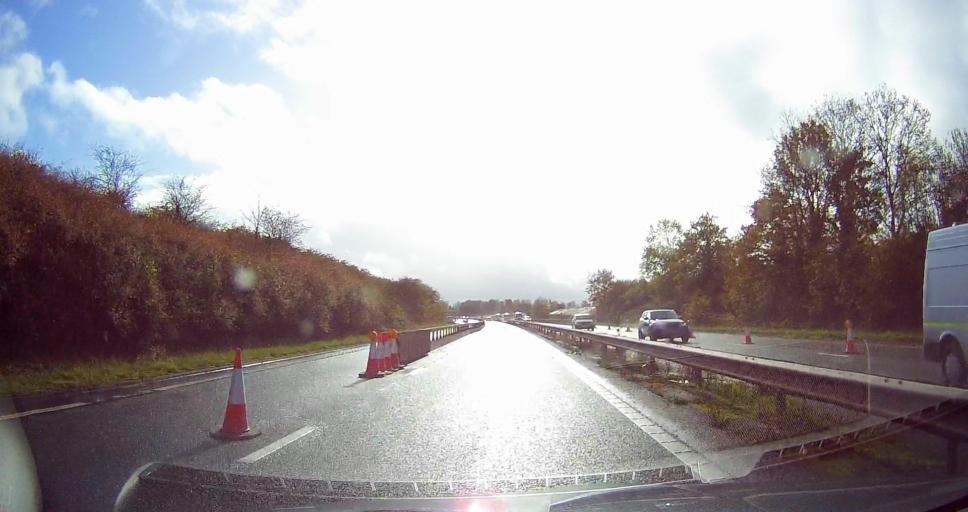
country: GB
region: England
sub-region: Warwickshire
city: Curdworth
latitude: 52.5386
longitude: -1.7785
